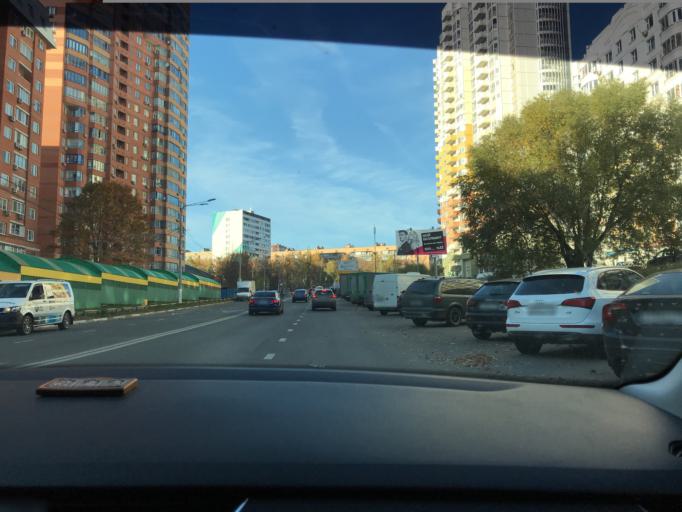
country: RU
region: Moscow
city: Khimki
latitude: 55.8852
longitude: 37.4272
